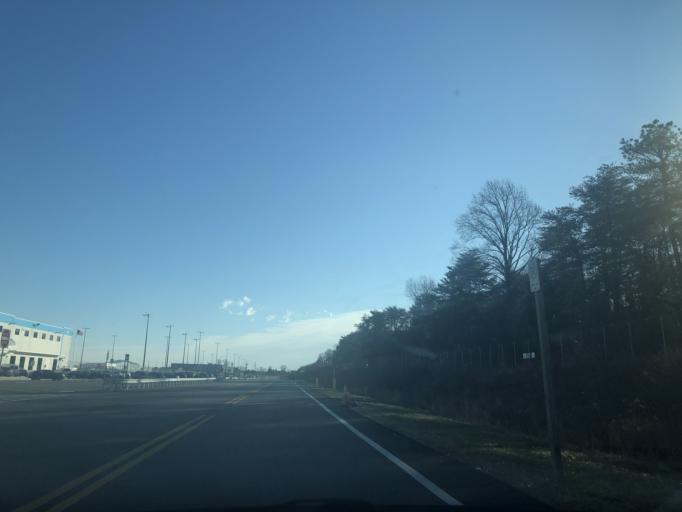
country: US
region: Maryland
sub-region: Anne Arundel County
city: Severn
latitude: 39.1705
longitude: -76.6847
